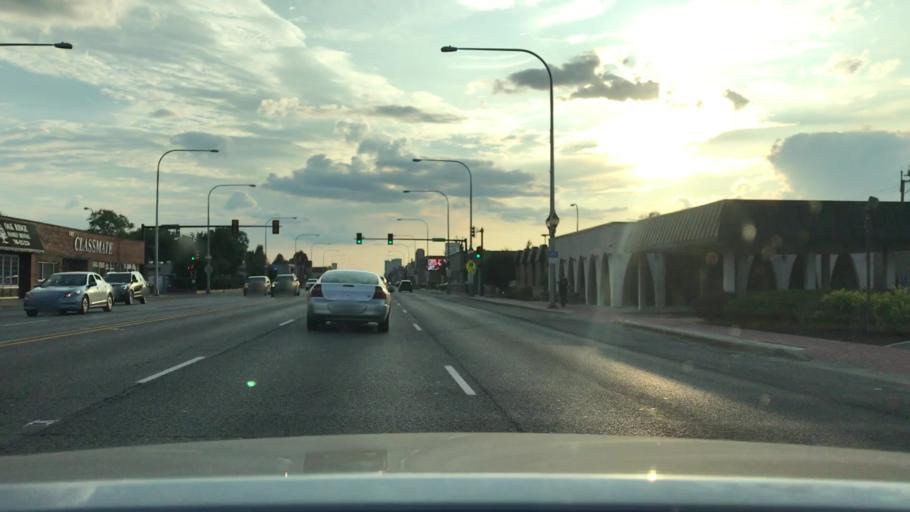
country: US
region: Illinois
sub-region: Cook County
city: Evergreen Park
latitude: 41.7207
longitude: -87.7118
